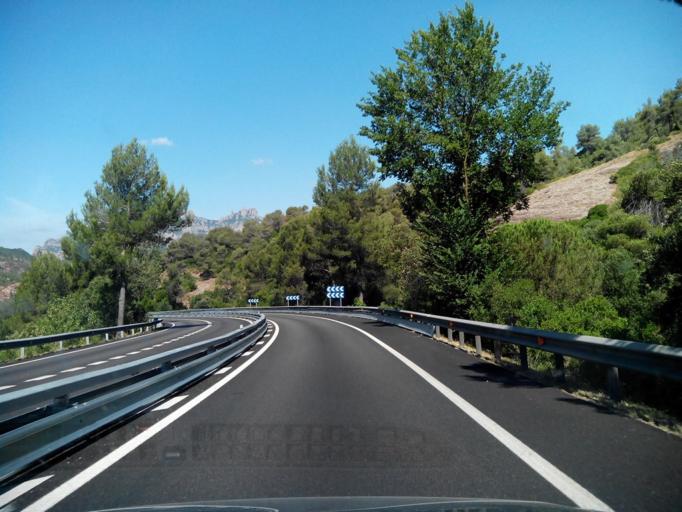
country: ES
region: Catalonia
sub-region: Provincia de Barcelona
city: Viladecavalls
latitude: 41.5846
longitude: 1.9340
